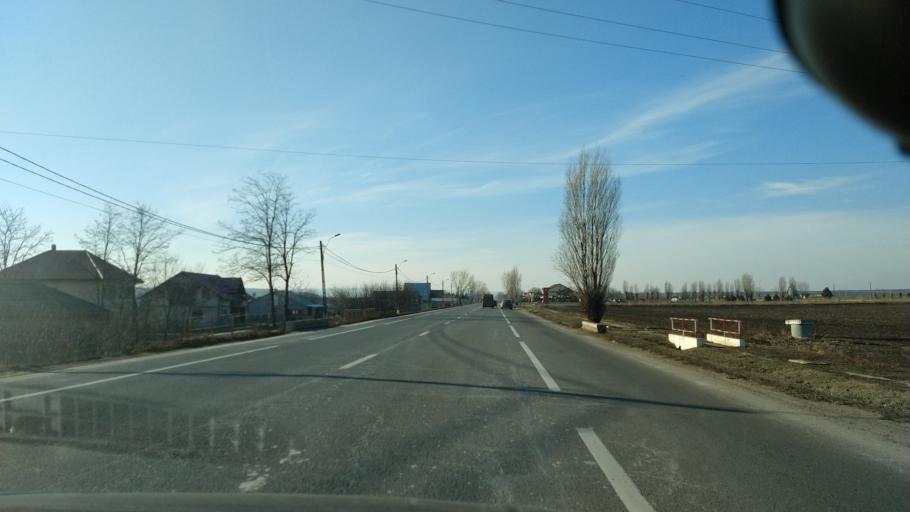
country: RO
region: Iasi
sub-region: Comuna Ion Neculce
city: Razboieni
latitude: 47.2201
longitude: 27.0683
